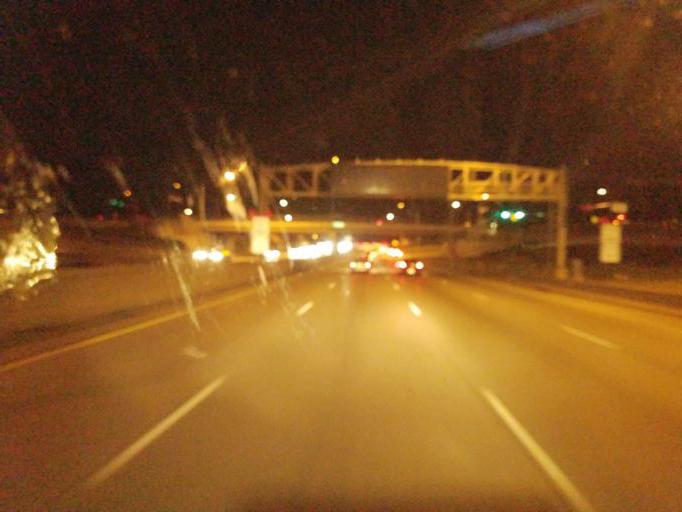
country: US
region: Iowa
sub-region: Polk County
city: Windsor Heights
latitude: 41.5930
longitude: -93.6609
